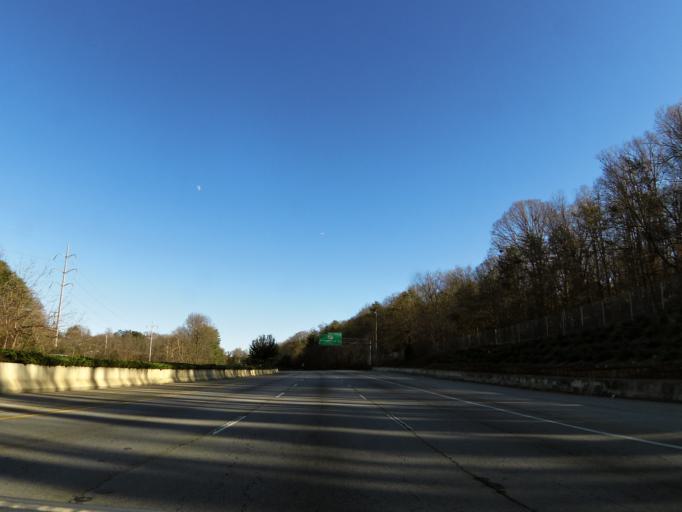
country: US
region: South Carolina
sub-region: Greenville County
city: Greenville
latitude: 34.8531
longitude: -82.3759
